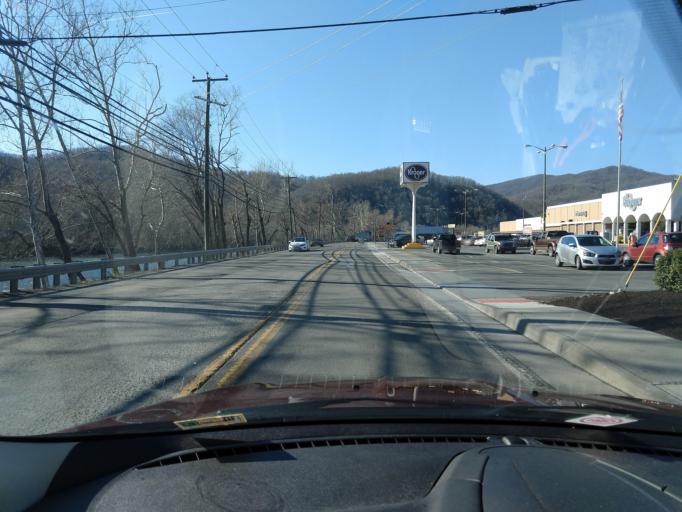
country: US
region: West Virginia
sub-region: Summers County
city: Hinton
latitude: 37.6591
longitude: -80.8909
